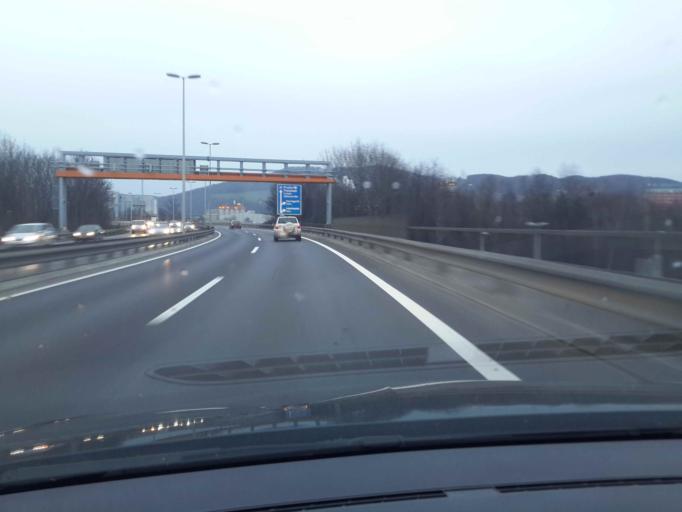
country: AT
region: Upper Austria
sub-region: Linz Stadt
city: Linz
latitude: 48.2858
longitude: 14.3168
